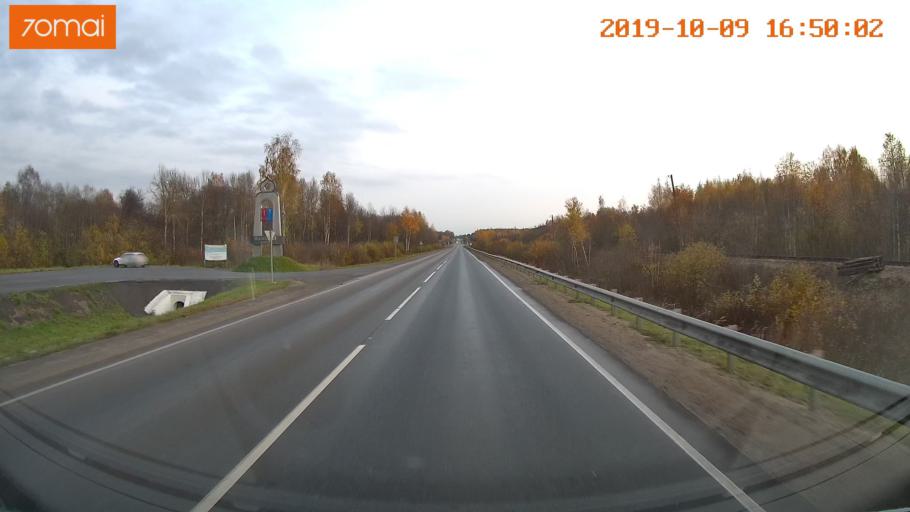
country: RU
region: Kostroma
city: Volgorechensk
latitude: 57.4066
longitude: 41.2036
